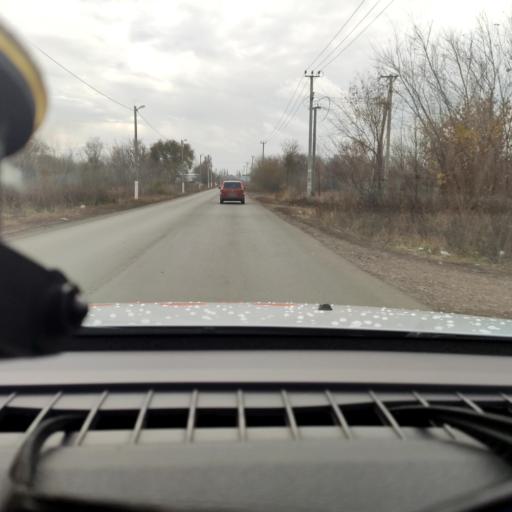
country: RU
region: Samara
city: Chapayevsk
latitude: 52.9915
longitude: 49.7297
